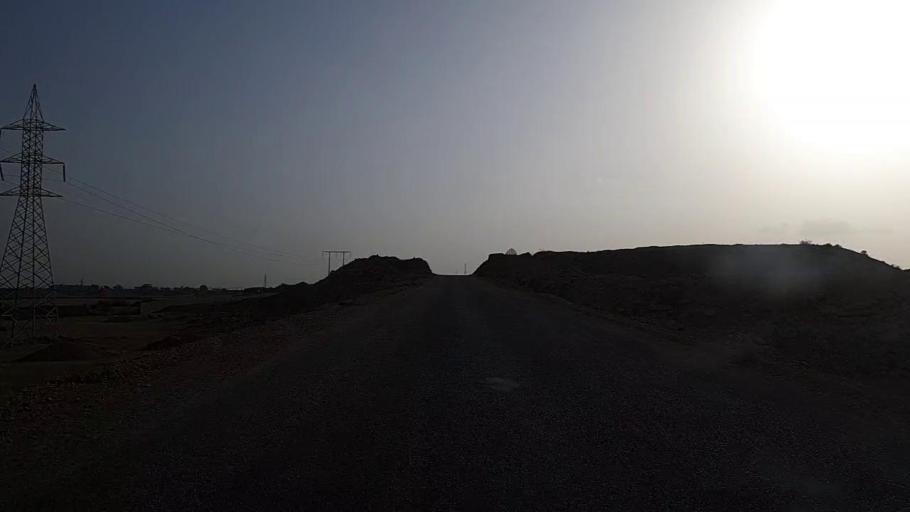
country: PK
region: Sindh
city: Thatta
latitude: 25.1856
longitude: 67.8326
